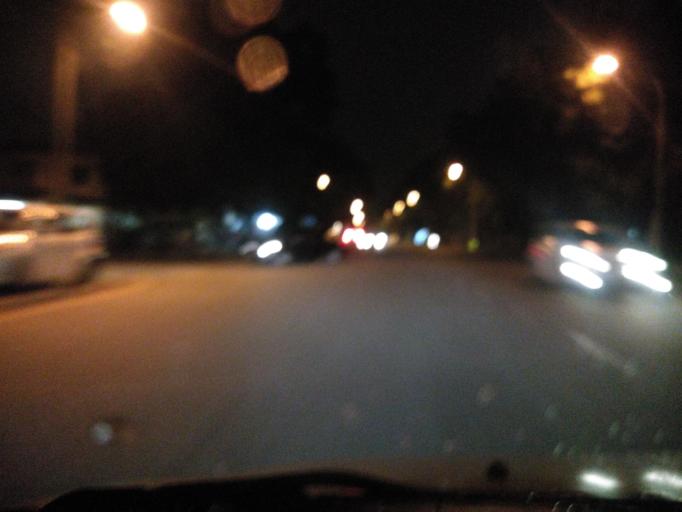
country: MY
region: Penang
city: Perai
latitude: 5.3964
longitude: 100.4019
